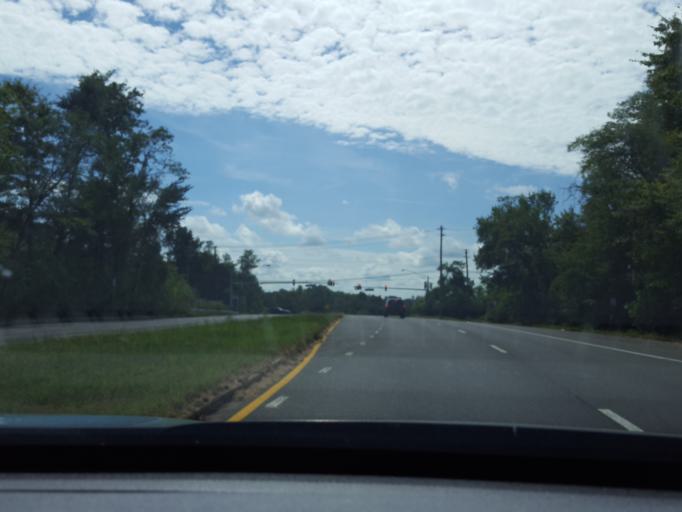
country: US
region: Maryland
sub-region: Prince George's County
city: Mellwood
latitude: 38.8116
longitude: -76.8248
